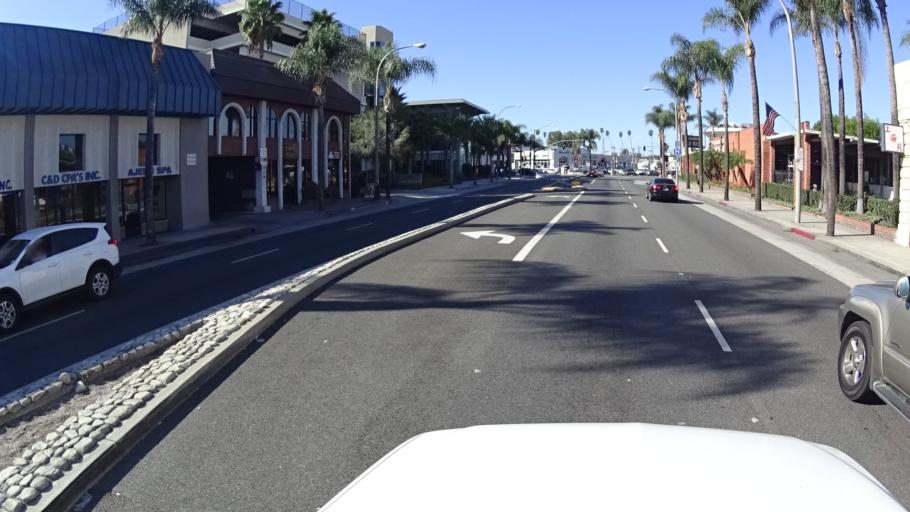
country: US
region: California
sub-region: Los Angeles County
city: Alhambra
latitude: 34.0921
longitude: -118.1334
